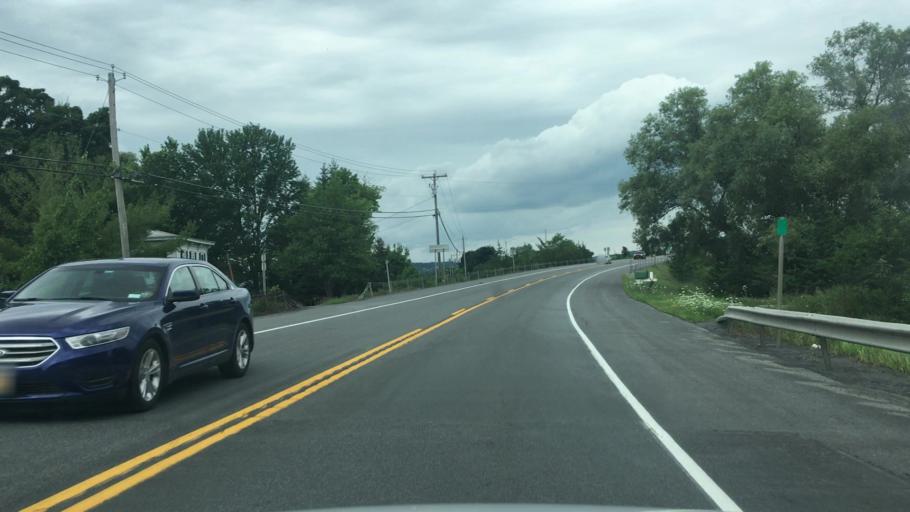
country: US
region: New York
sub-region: Schoharie County
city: Schoharie
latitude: 42.7041
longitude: -74.3110
